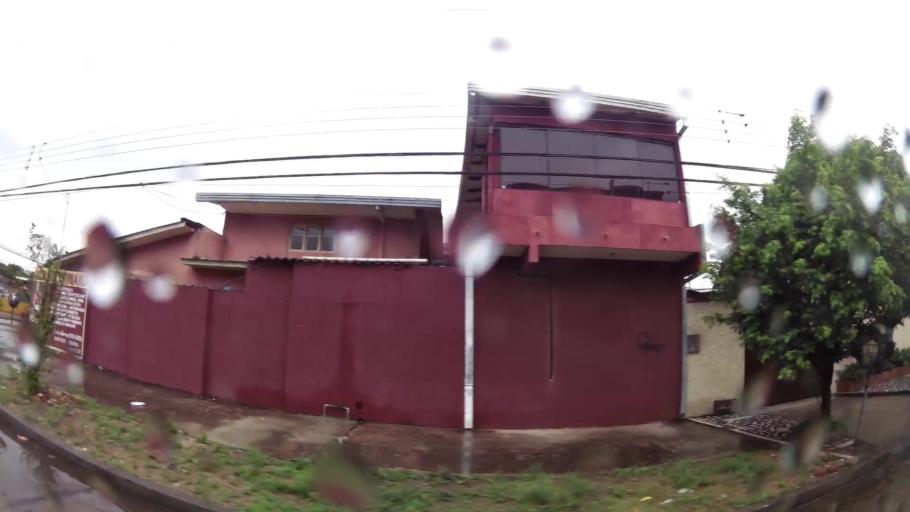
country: BO
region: Santa Cruz
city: Santa Cruz de la Sierra
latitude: -17.8079
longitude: -63.1969
